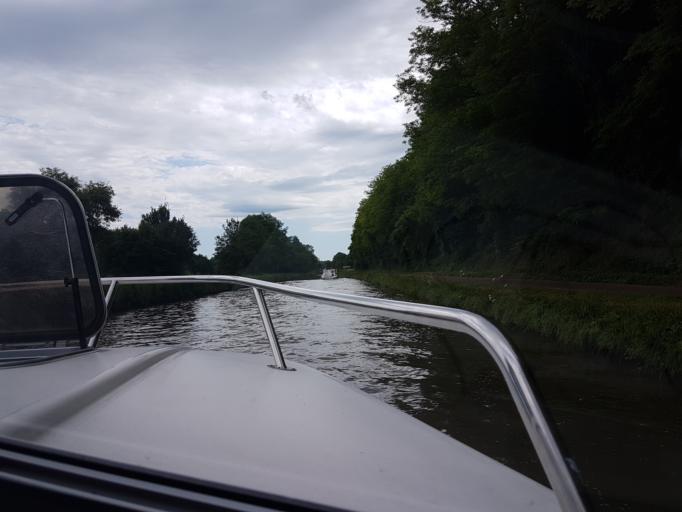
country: FR
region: Bourgogne
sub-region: Departement de la Nievre
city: Clamecy
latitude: 47.4866
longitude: 3.5243
